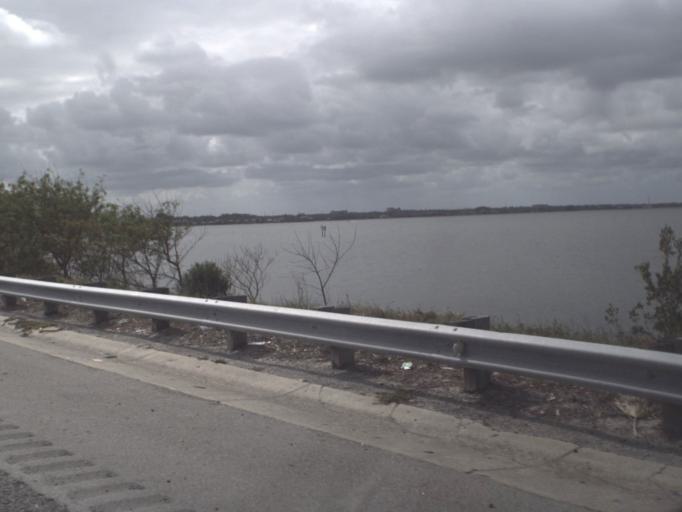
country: US
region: Florida
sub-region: Brevard County
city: South Patrick Shores
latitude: 28.2073
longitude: -80.6443
